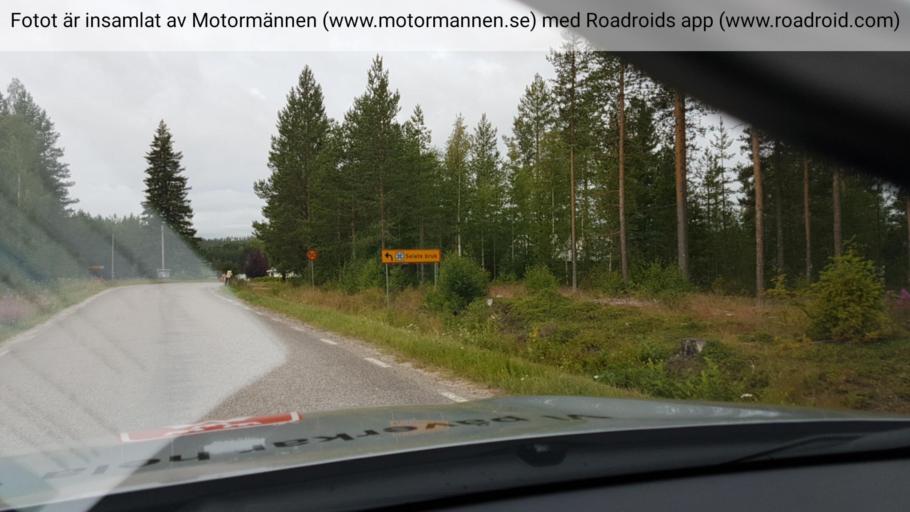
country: SE
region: Norrbotten
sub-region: Bodens Kommun
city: Saevast
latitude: 65.6673
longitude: 21.6778
